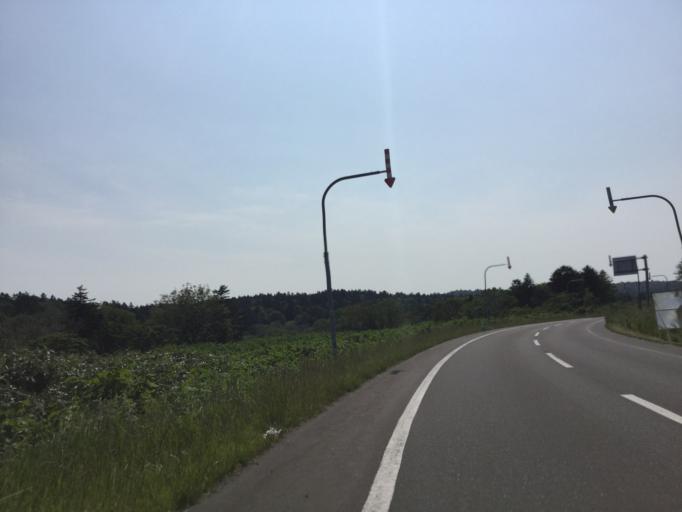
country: JP
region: Hokkaido
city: Makubetsu
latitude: 45.4051
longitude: 142.0402
